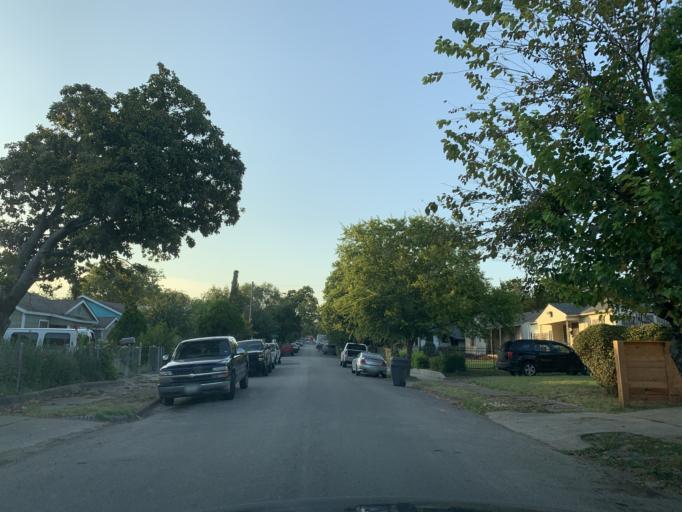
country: US
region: Texas
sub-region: Dallas County
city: Dallas
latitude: 32.7088
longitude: -96.8078
